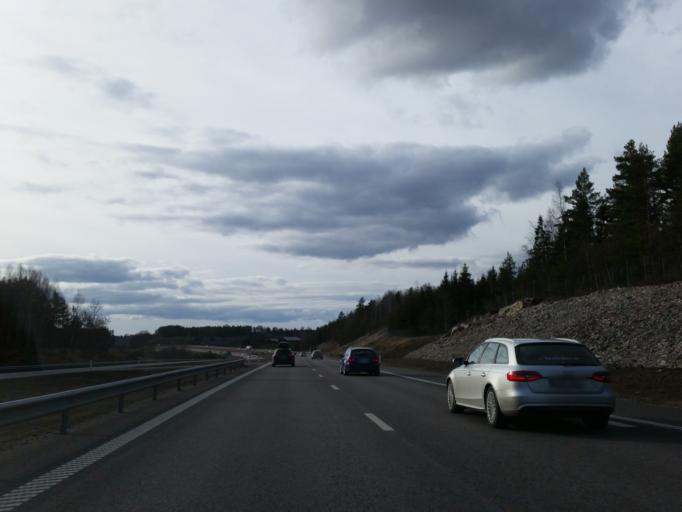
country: SE
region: Soedermanland
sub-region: Nykopings Kommun
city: Stigtomta
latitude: 58.7565
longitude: 16.7221
